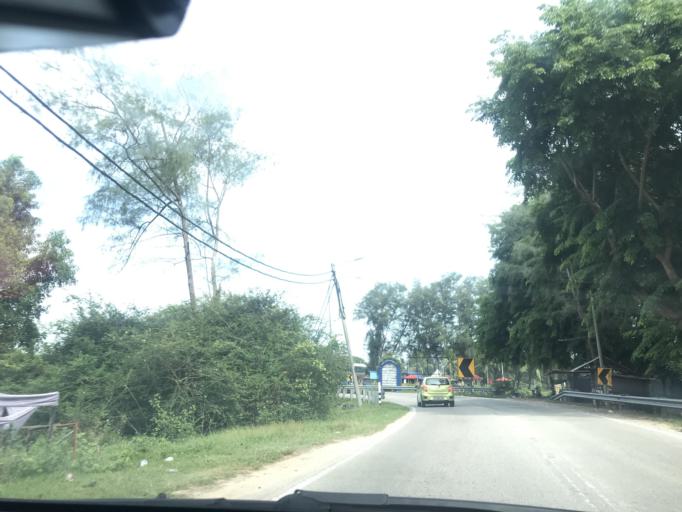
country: MY
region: Kelantan
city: Tumpat
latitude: 6.2064
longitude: 102.1457
